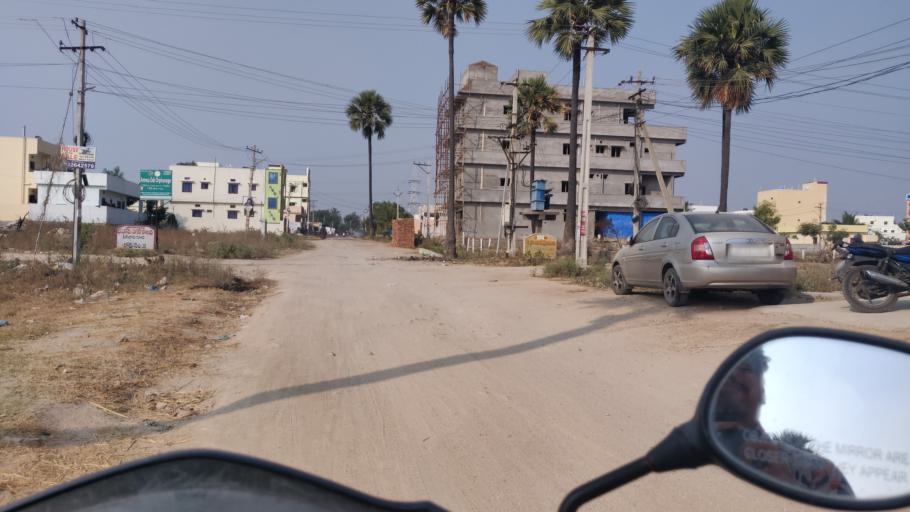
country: IN
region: Telangana
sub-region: Rangareddi
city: Uppal Kalan
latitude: 17.3946
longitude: 78.6050
